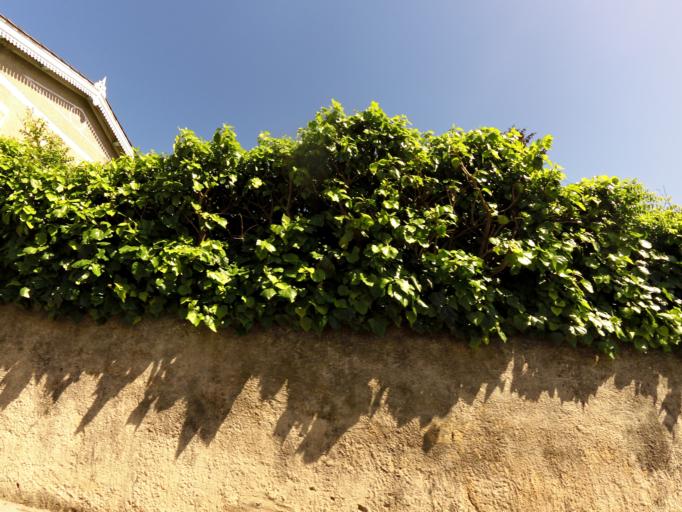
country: FR
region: Languedoc-Roussillon
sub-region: Departement de l'Herault
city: Castries
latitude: 43.6782
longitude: 3.9840
